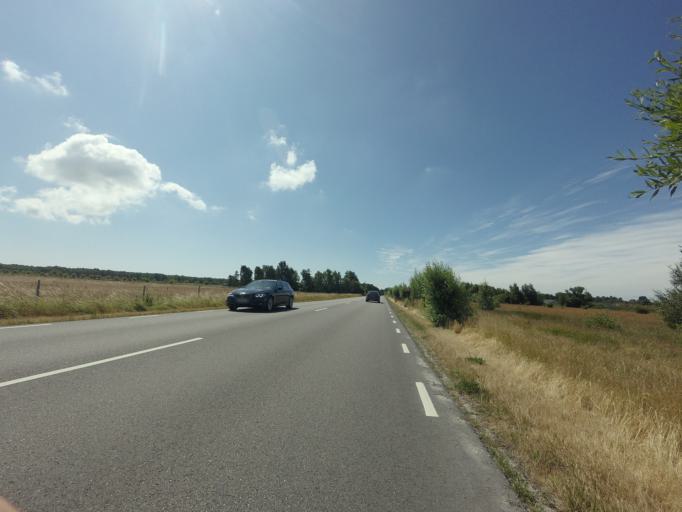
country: SE
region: Skane
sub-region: Vellinge Kommun
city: Skanor med Falsterbo
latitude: 55.4139
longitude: 12.8670
